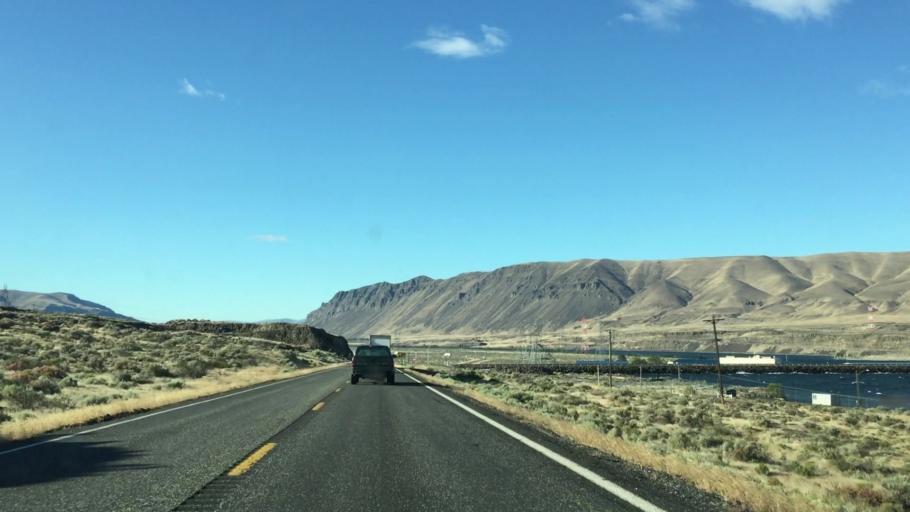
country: US
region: Washington
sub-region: Grant County
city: Mattawa
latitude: 46.8831
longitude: -119.9551
